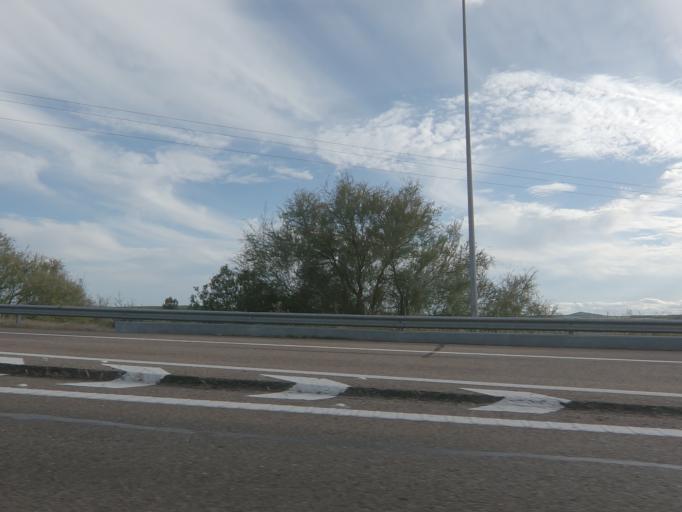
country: PT
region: Portalegre
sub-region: Elvas
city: Elvas
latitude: 38.8908
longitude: -7.1146
